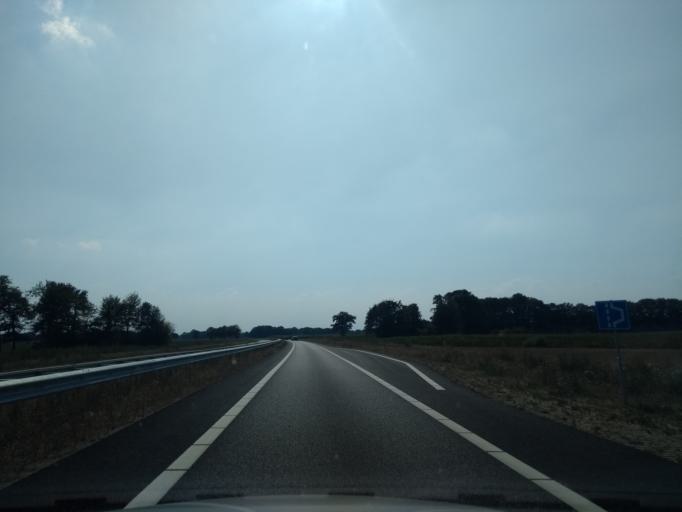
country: NL
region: Overijssel
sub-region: Gemeente Haaksbergen
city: Haaksbergen
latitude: 52.1801
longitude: 6.7294
